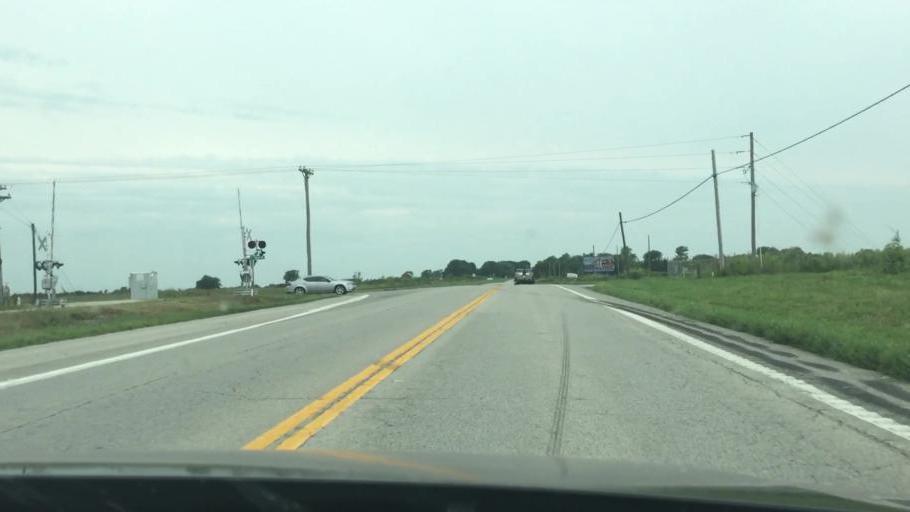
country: US
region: Missouri
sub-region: Pettis County
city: Sedalia
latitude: 38.6962
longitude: -93.1712
